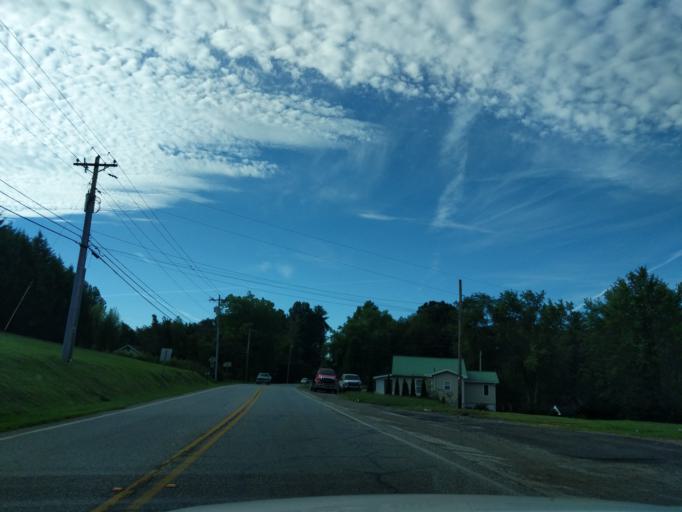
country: US
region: Georgia
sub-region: Fannin County
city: McCaysville
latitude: 34.9721
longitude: -84.3712
